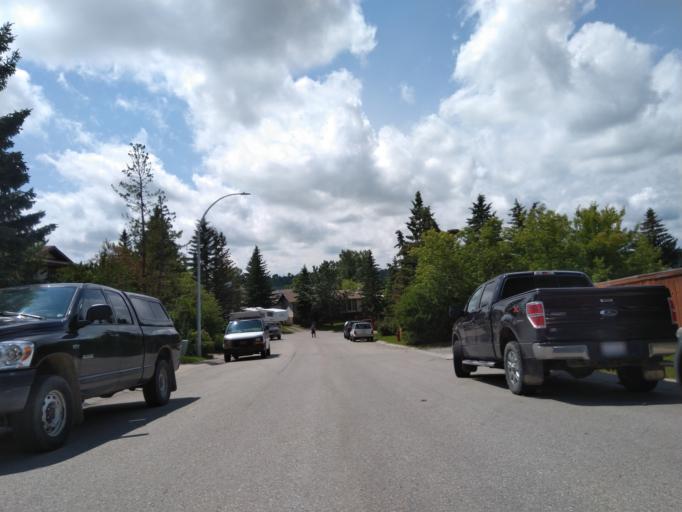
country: CA
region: Alberta
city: Cochrane
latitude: 51.1849
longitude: -114.4785
